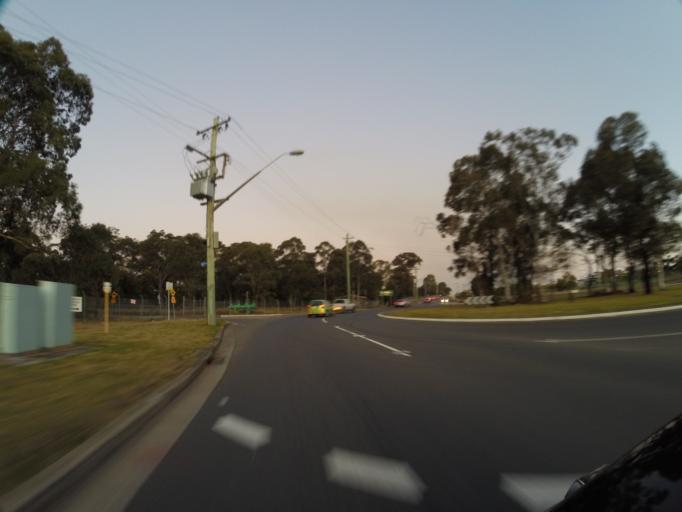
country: AU
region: New South Wales
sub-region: Liverpool
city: Holsworthy
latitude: -33.9608
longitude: 150.9596
